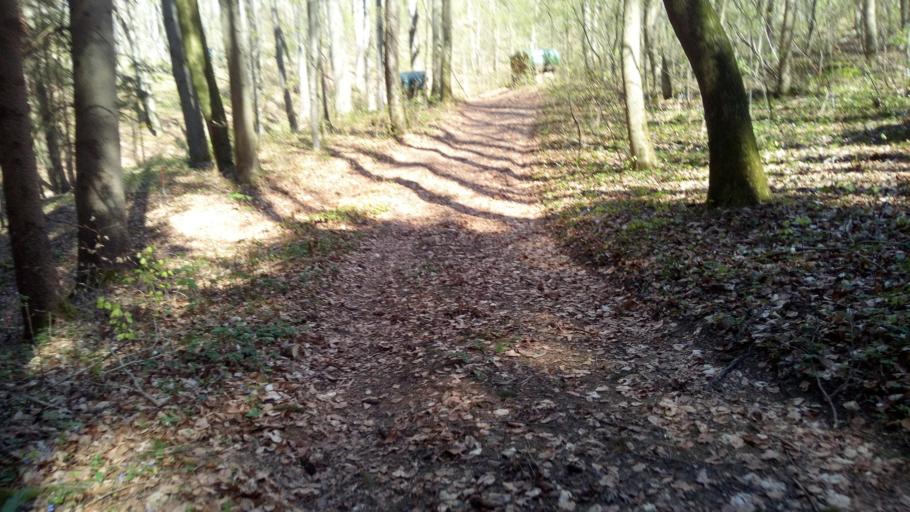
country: DE
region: Baden-Wuerttemberg
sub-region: Regierungsbezirk Stuttgart
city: Donzdorf
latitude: 48.7102
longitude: 9.8388
